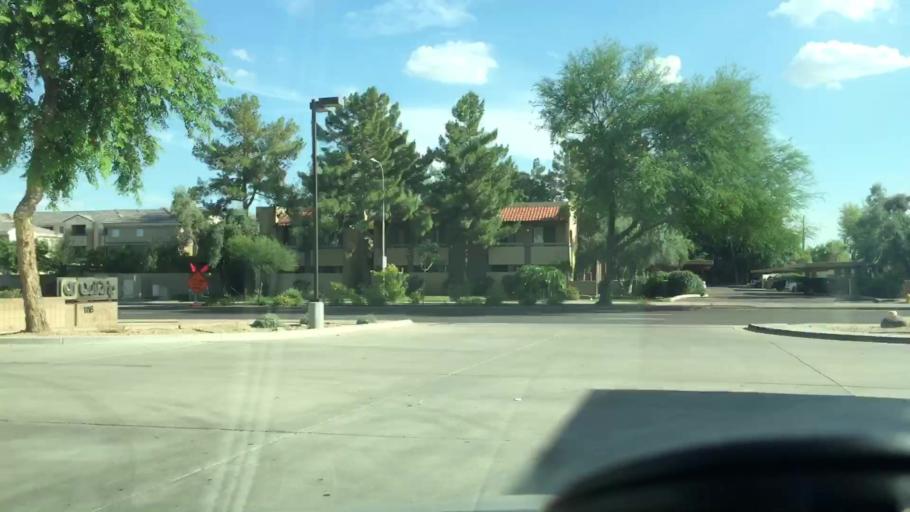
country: US
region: Arizona
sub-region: Maricopa County
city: Tempe
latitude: 33.4080
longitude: -111.9218
